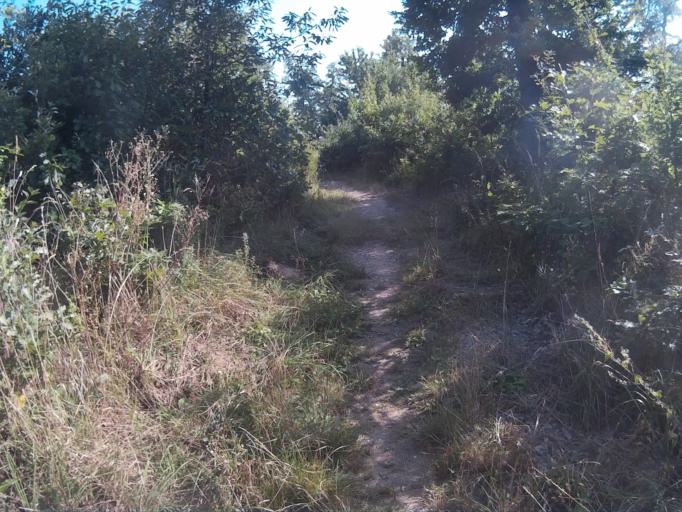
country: HU
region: Vas
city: Koszeg
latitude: 47.3995
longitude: 16.5280
